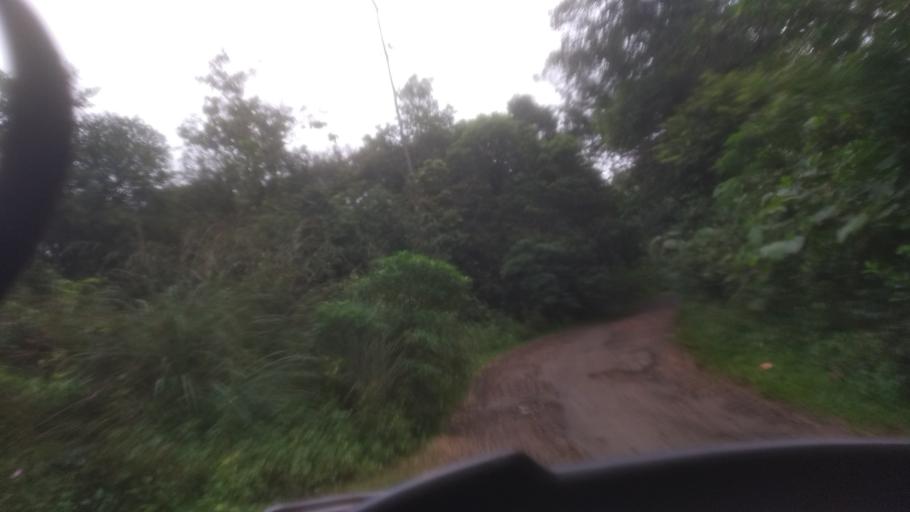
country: IN
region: Tamil Nadu
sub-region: Theni
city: Kombai
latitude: 9.8911
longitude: 77.2177
